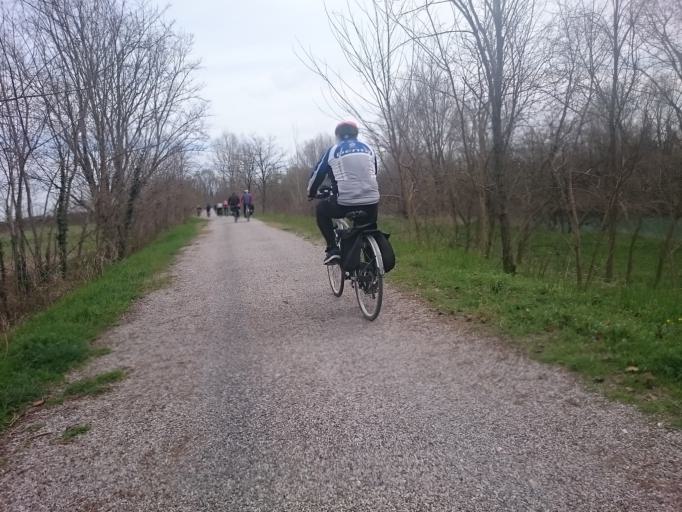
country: IT
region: Veneto
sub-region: Provincia di Padova
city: Limena
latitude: 45.4792
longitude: 11.8503
